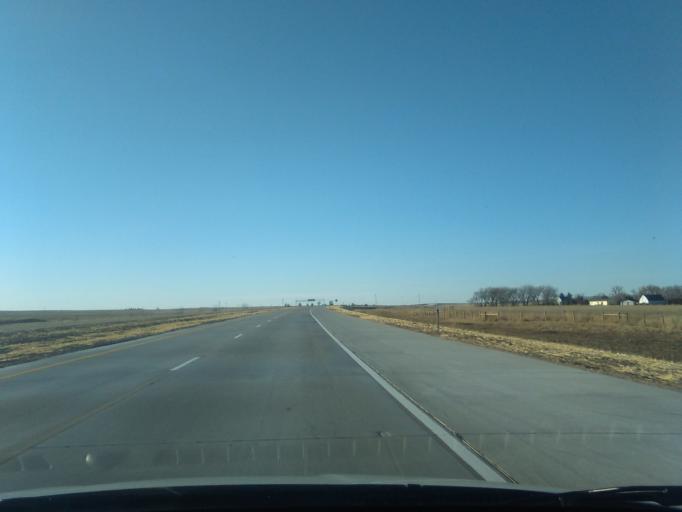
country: US
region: Nebraska
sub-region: Deuel County
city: Chappell
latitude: 41.0890
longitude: -102.5076
